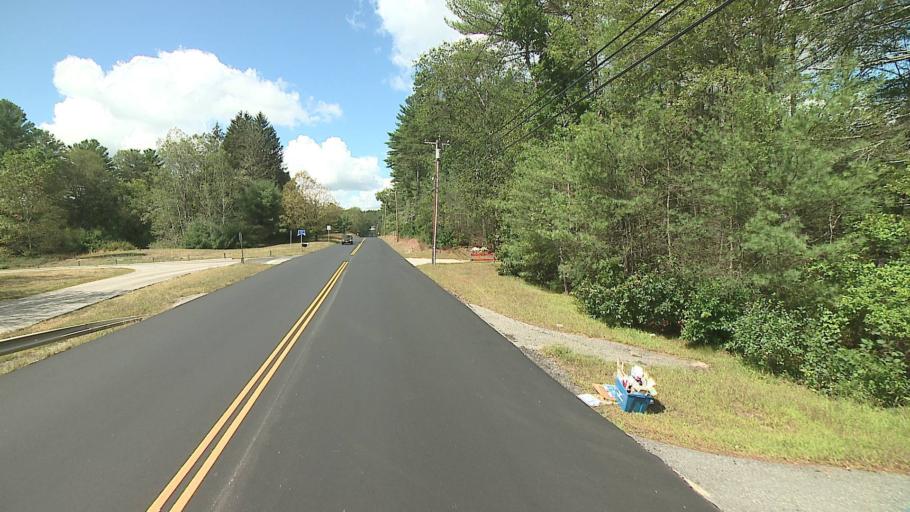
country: US
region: Connecticut
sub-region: Windham County
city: Thompson
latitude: 41.9188
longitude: -71.8301
